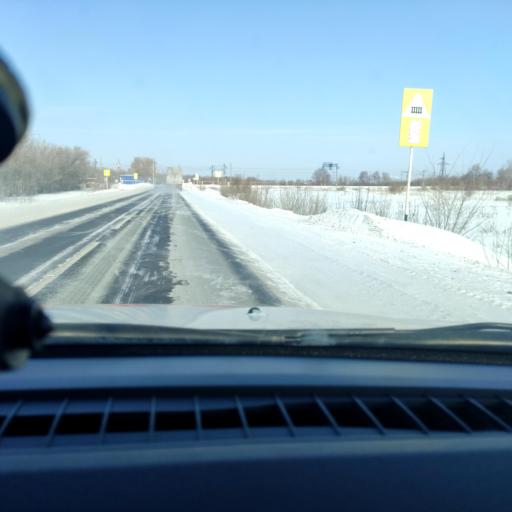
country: RU
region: Samara
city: Smyshlyayevka
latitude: 53.1686
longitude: 50.4571
